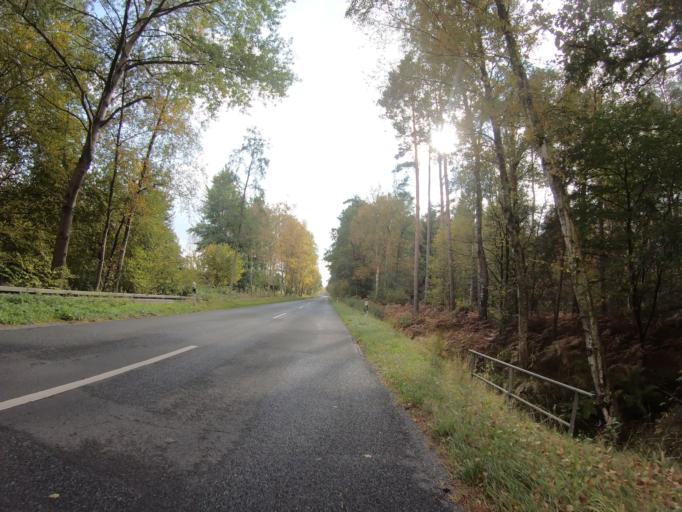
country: DE
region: Lower Saxony
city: Schoneworde
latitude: 52.5958
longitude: 10.6411
